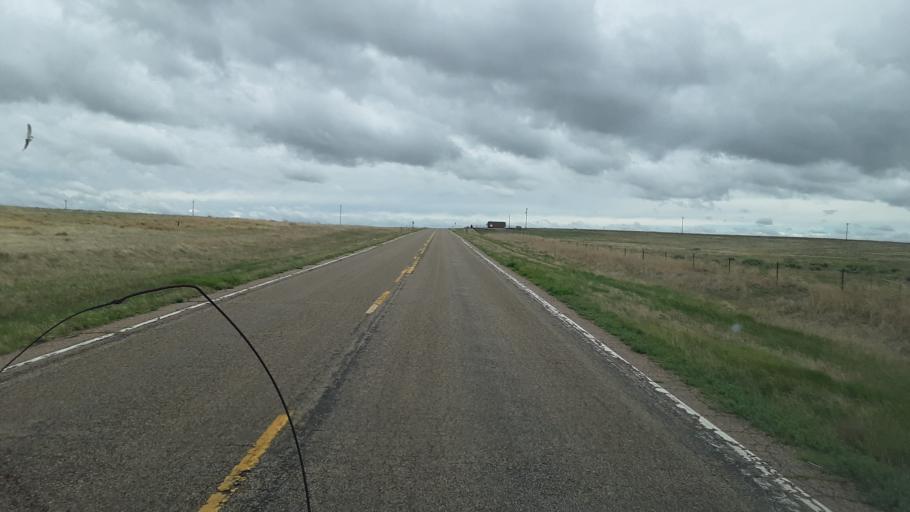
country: US
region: Colorado
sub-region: Lincoln County
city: Hugo
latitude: 38.8511
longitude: -103.6217
